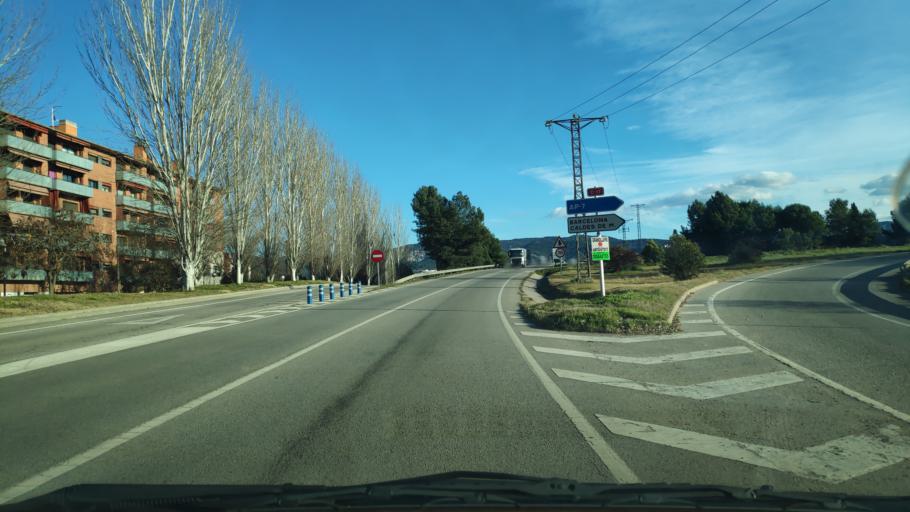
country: ES
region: Catalonia
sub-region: Provincia de Barcelona
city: Mollet del Valles
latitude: 41.5332
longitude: 2.2142
